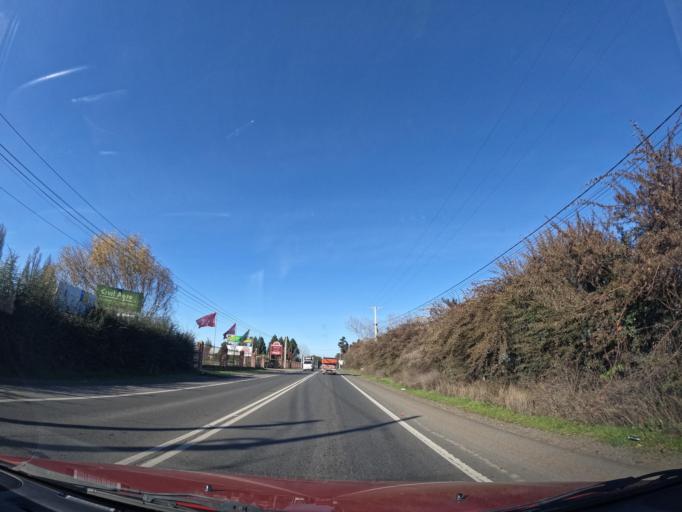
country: CL
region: Maule
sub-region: Provincia de Linares
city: San Javier
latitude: -35.6235
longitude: -71.7583
